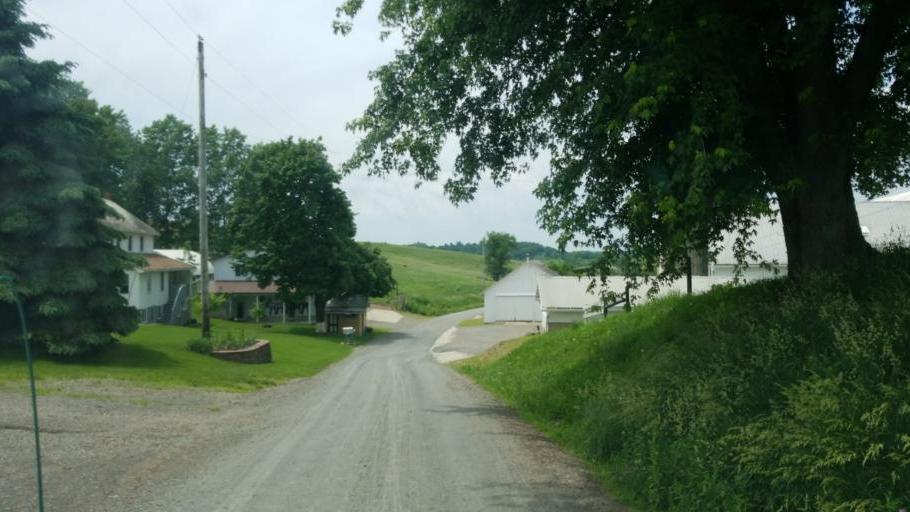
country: US
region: Ohio
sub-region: Tuscarawas County
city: Sugarcreek
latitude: 40.4814
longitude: -81.7880
